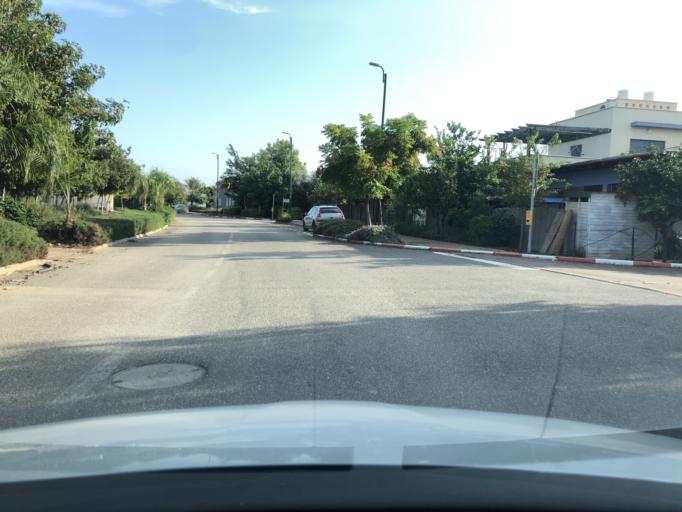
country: IL
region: Northern District
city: Yavne'el
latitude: 32.6573
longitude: 35.5770
